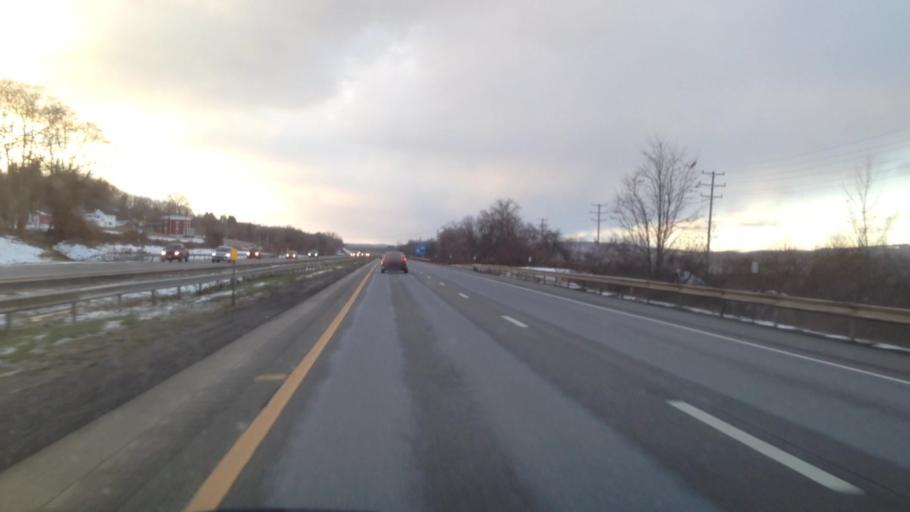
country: US
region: New York
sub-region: Herkimer County
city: Herkimer
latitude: 43.0141
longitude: -74.9342
